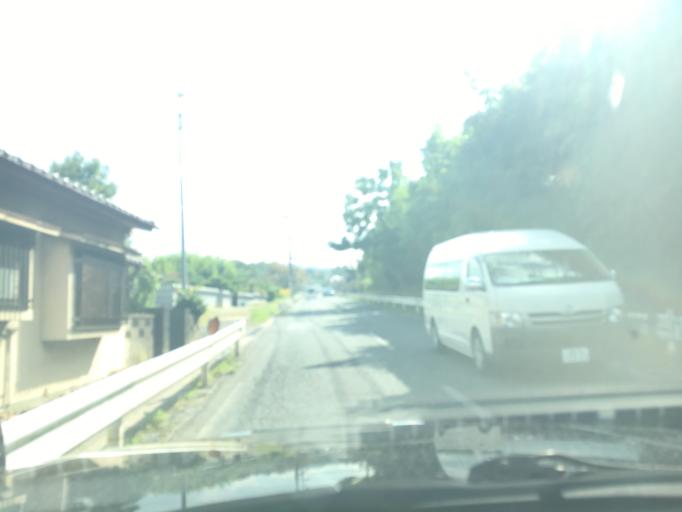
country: JP
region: Nara
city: Nara-shi
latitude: 34.7065
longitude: 135.8328
